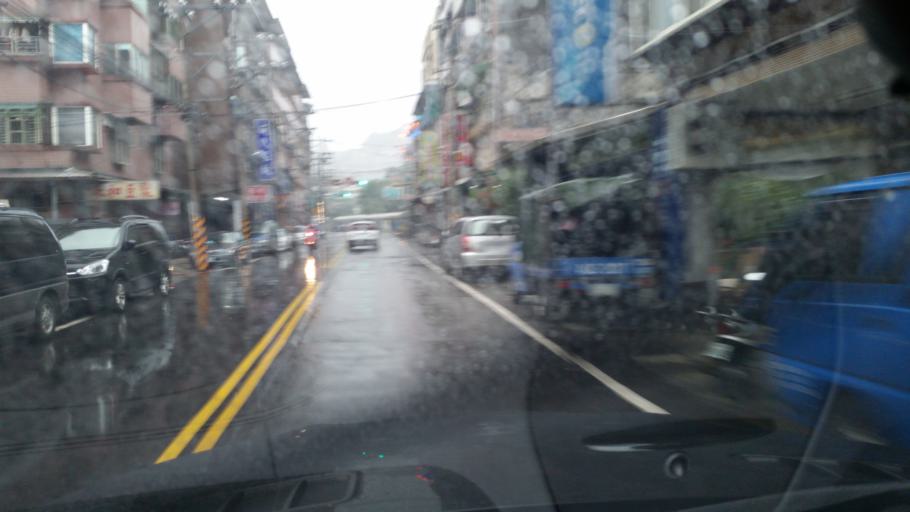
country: TW
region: Taiwan
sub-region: Keelung
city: Keelung
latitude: 25.1442
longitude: 121.7669
